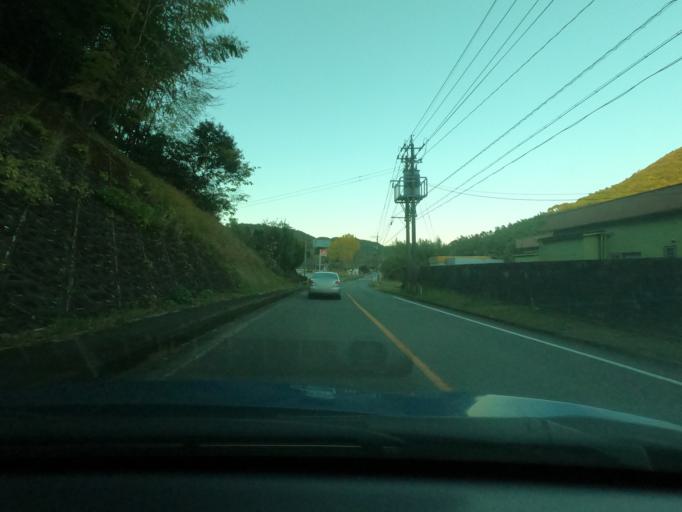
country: JP
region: Kagoshima
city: Satsumasendai
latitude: 31.8039
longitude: 130.4810
